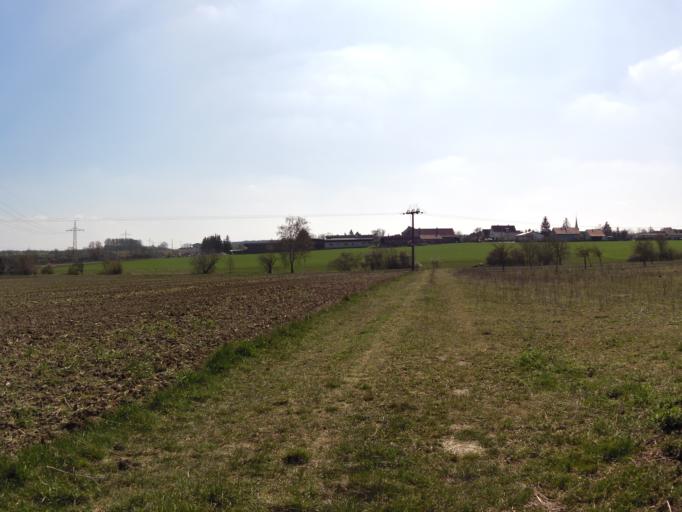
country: DE
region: Bavaria
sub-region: Regierungsbezirk Unterfranken
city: Biebelried
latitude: 49.7350
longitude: 10.0904
